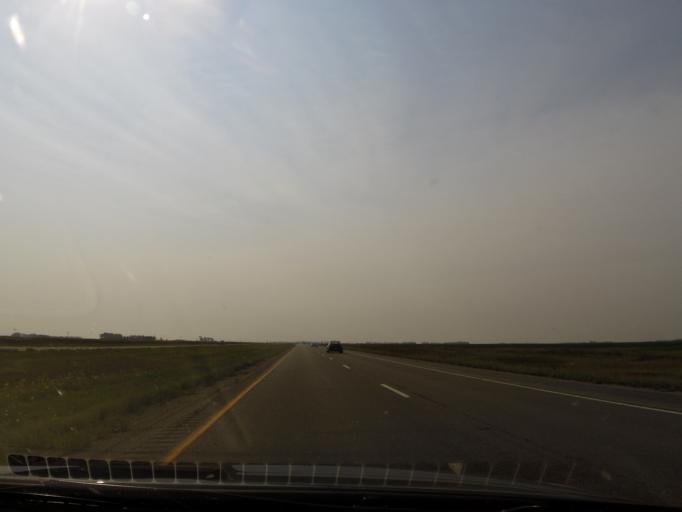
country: US
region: North Dakota
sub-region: Traill County
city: Hillsboro
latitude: 47.1900
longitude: -96.9886
